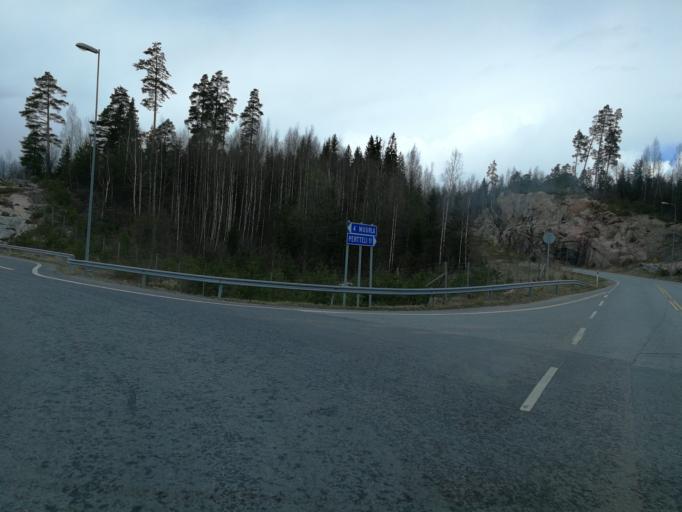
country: FI
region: Varsinais-Suomi
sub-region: Salo
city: Muurla
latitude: 60.3802
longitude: 23.3204
